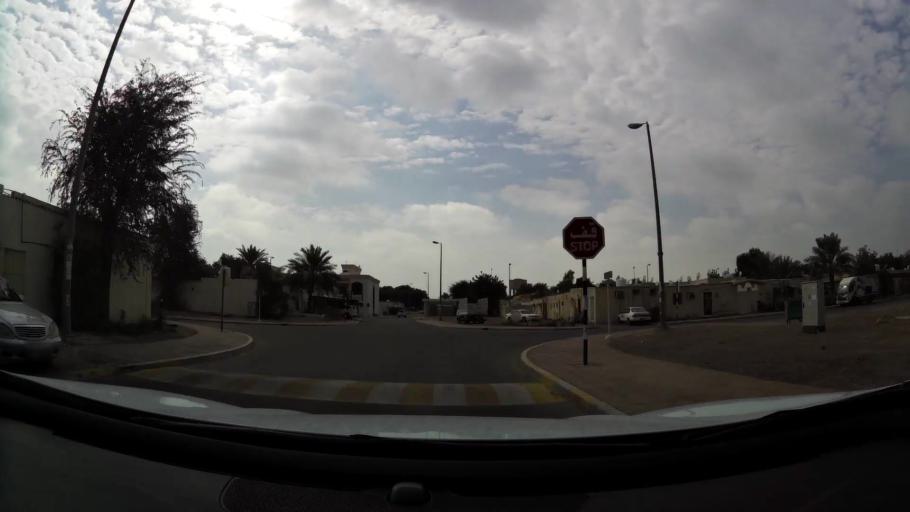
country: AE
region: Abu Dhabi
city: Al Ain
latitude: 24.2263
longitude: 55.7535
